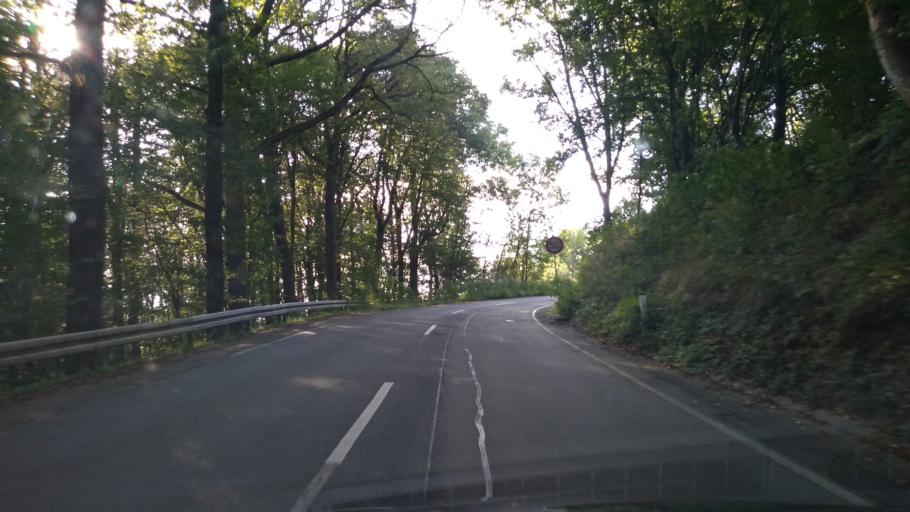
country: DE
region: North Rhine-Westphalia
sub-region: Regierungsbezirk Koln
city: Engelskirchen
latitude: 50.9770
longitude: 7.4441
